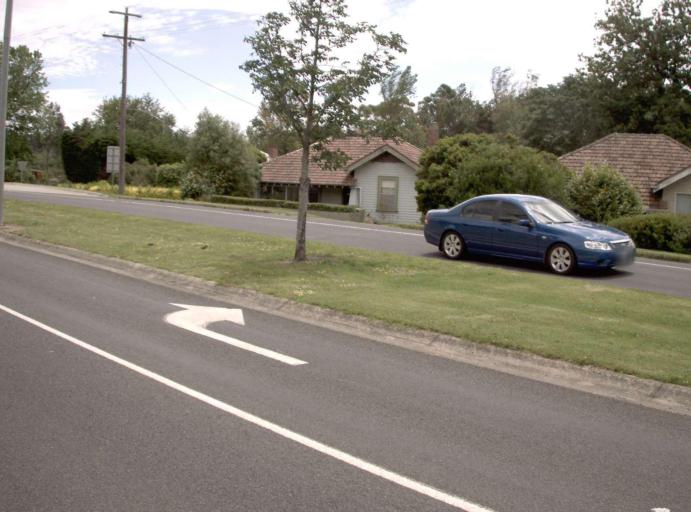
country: AU
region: Victoria
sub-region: Baw Baw
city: Warragul
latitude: -38.1571
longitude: 145.9193
